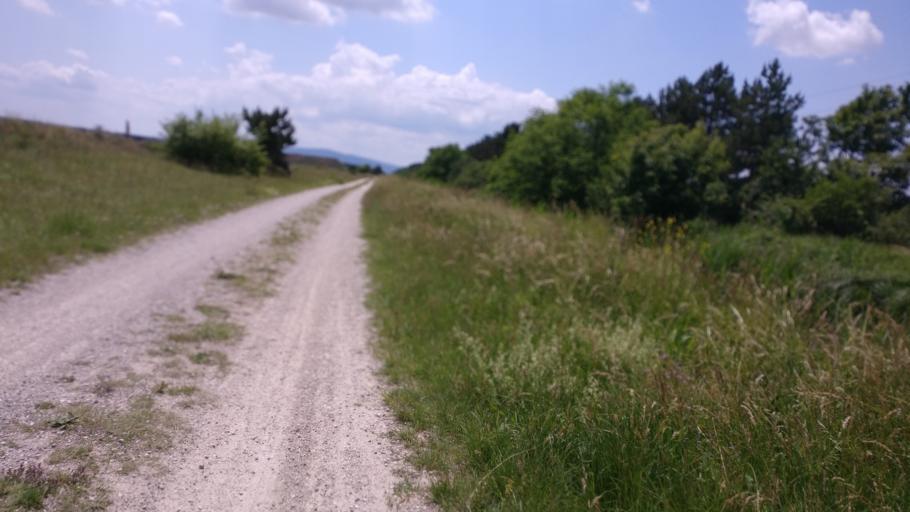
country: AT
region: Lower Austria
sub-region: Politischer Bezirk Wiener Neustadt
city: Sollenau
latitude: 47.8726
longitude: 16.2815
